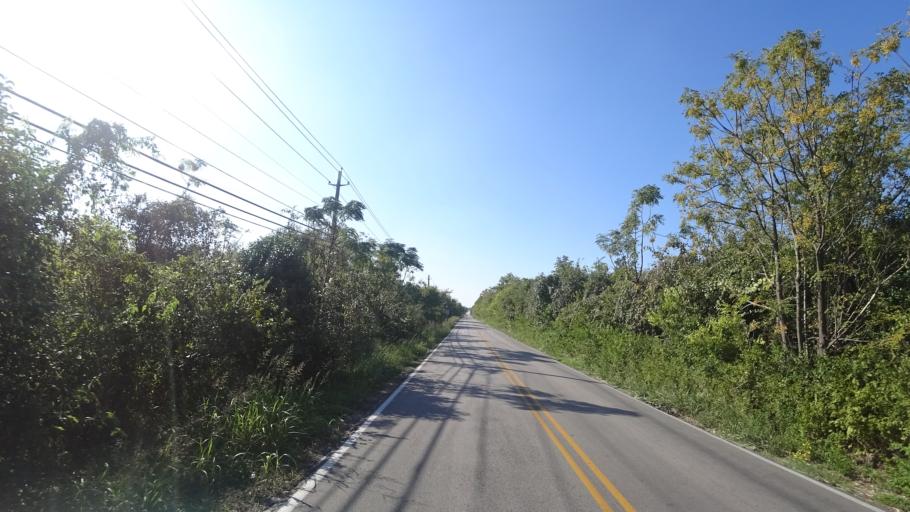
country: US
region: Texas
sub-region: Travis County
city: Manor
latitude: 30.3384
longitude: -97.6557
